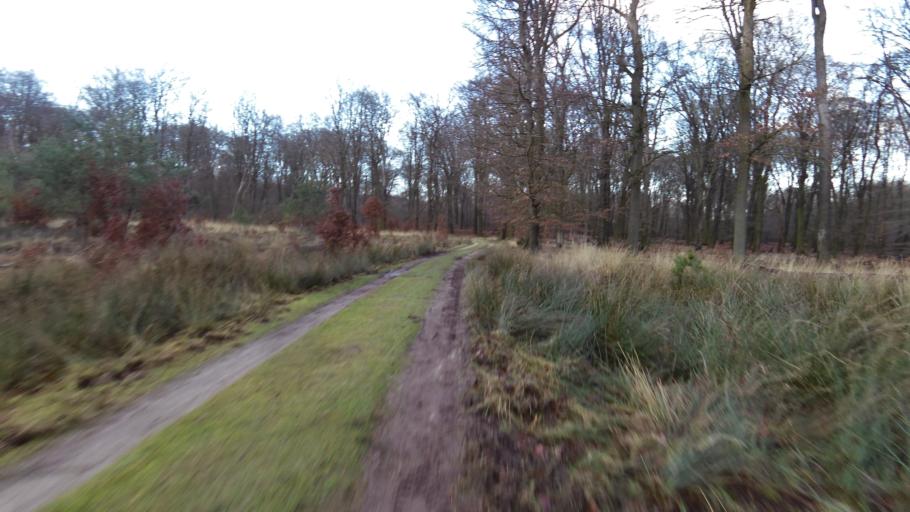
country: NL
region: Gelderland
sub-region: Gemeente Epe
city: Vaassen
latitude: 52.3131
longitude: 5.8762
